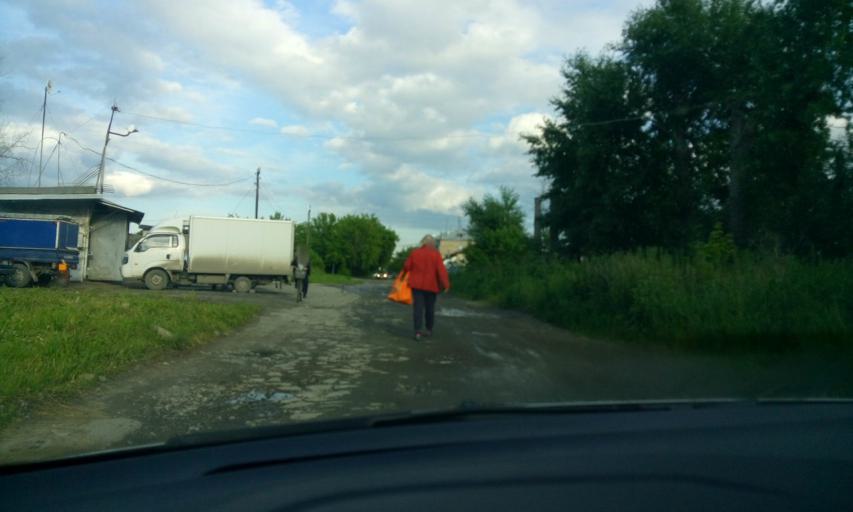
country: RU
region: Sverdlovsk
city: Yekaterinburg
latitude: 56.8897
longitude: 60.5616
